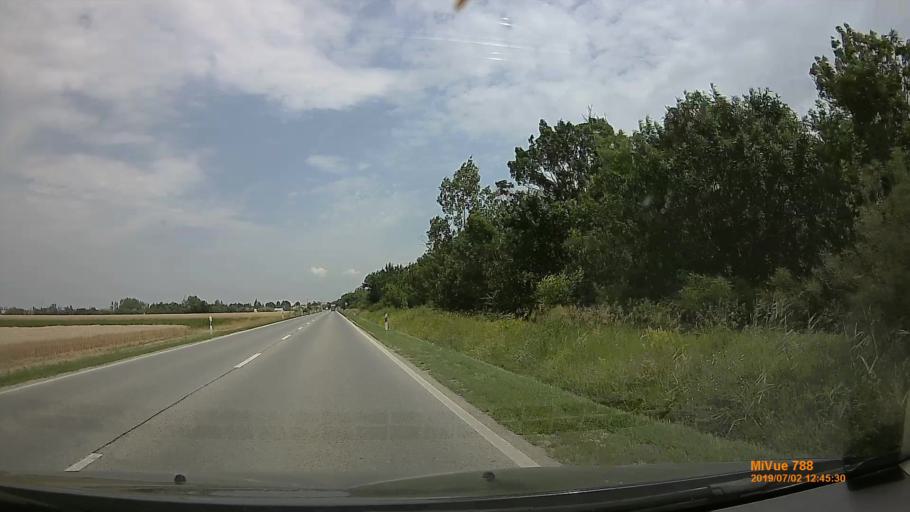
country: HU
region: Gyor-Moson-Sopron
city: Mosonmagyarovar
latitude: 47.8353
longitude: 17.2187
